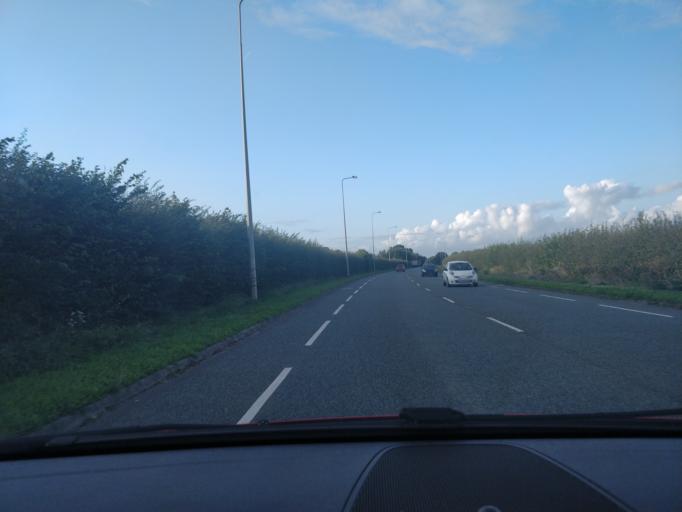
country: GB
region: England
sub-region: Lancashire
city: Tarleton
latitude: 53.6902
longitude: -2.8156
